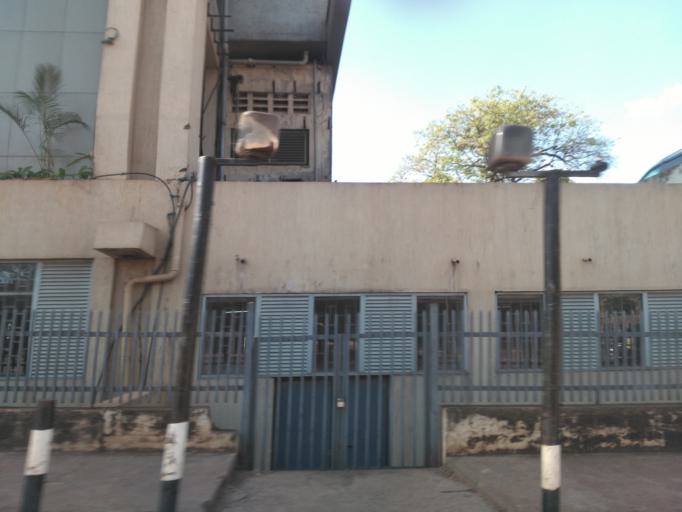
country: UG
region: Central Region
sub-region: Kampala District
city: Kampala
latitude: 0.3136
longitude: 32.5895
